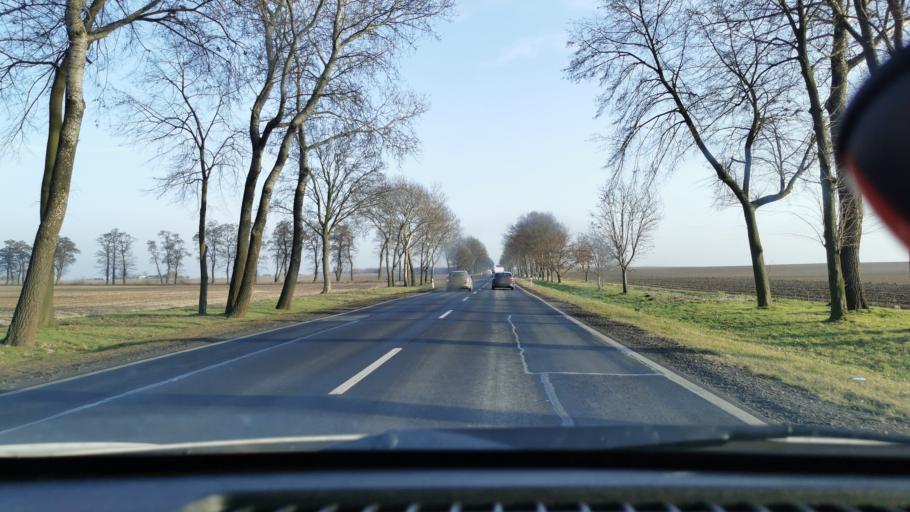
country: PL
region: Lodz Voivodeship
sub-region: Powiat sieradzki
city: Wroblew
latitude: 51.6210
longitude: 18.5838
